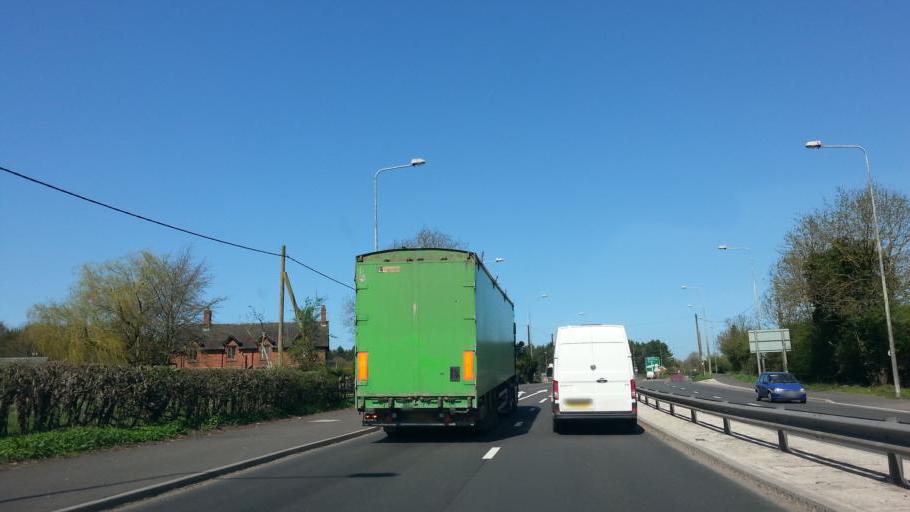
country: GB
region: England
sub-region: Staffordshire
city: Brewood
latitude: 52.6684
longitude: -2.1320
